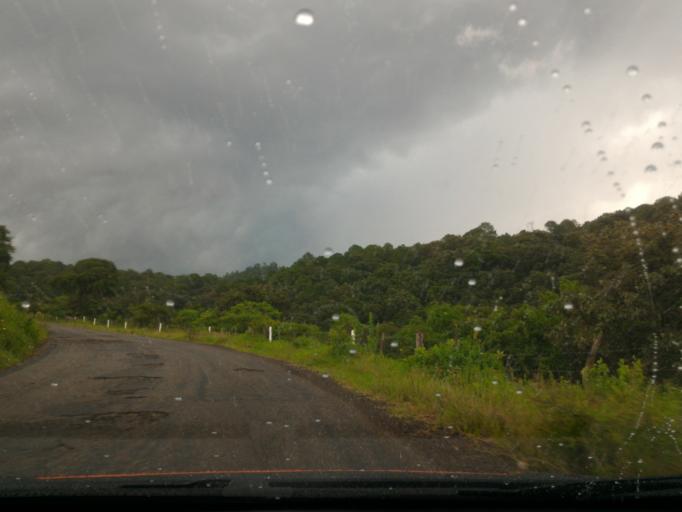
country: MX
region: Jalisco
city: San Andres Ixtlan
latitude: 19.8513
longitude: -103.4576
